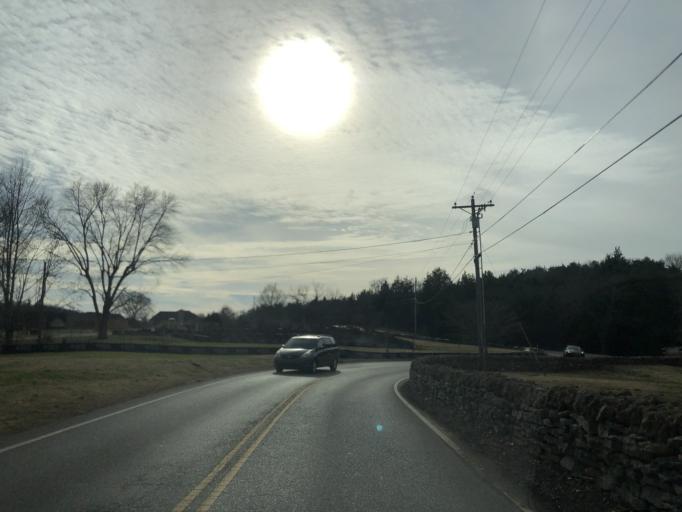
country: US
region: Tennessee
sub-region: Williamson County
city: Franklin
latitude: 35.9368
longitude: -86.9052
